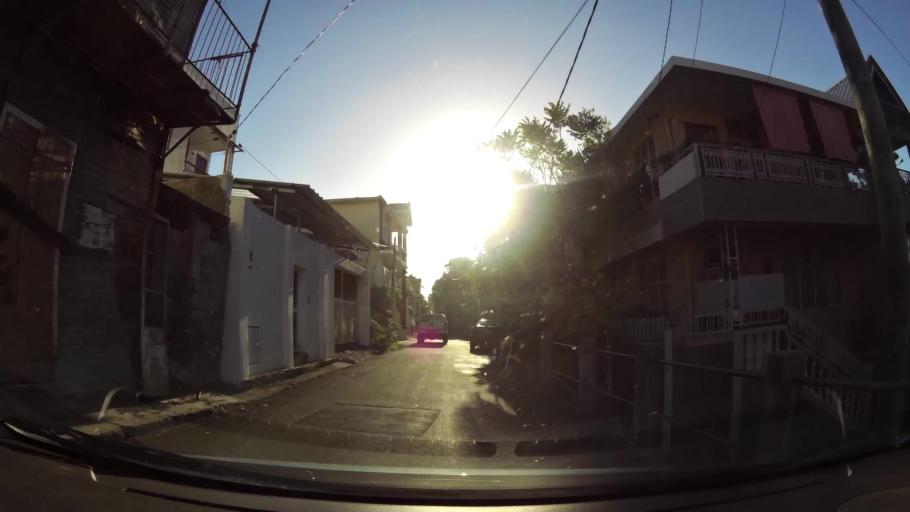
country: MU
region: Port Louis
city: Port Louis
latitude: -20.1671
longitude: 57.4950
